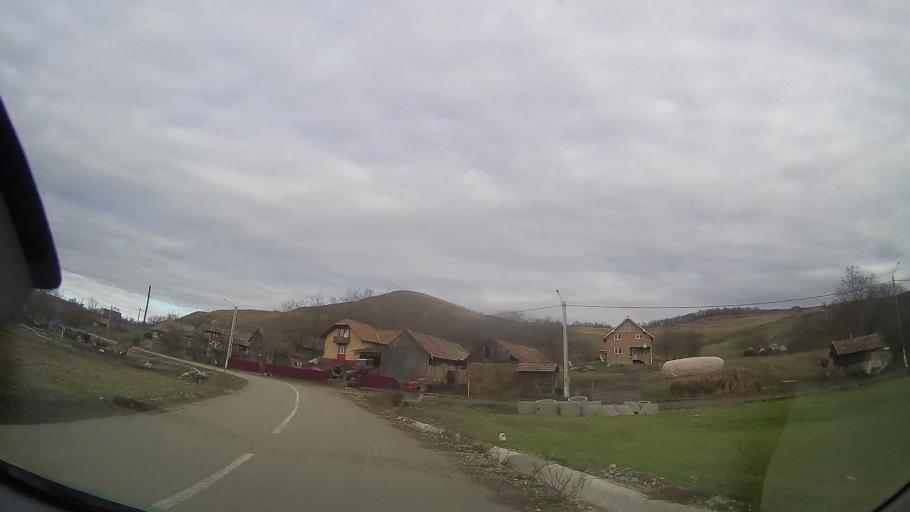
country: RO
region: Bistrita-Nasaud
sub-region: Comuna Micestii de Campie
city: Micestii de Campie
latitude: 46.8302
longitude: 24.3068
